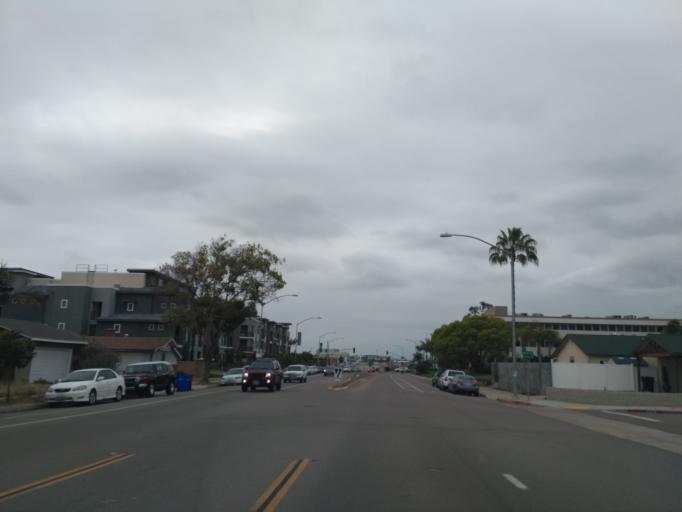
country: US
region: California
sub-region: San Diego County
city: San Diego
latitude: 32.8078
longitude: -117.1401
